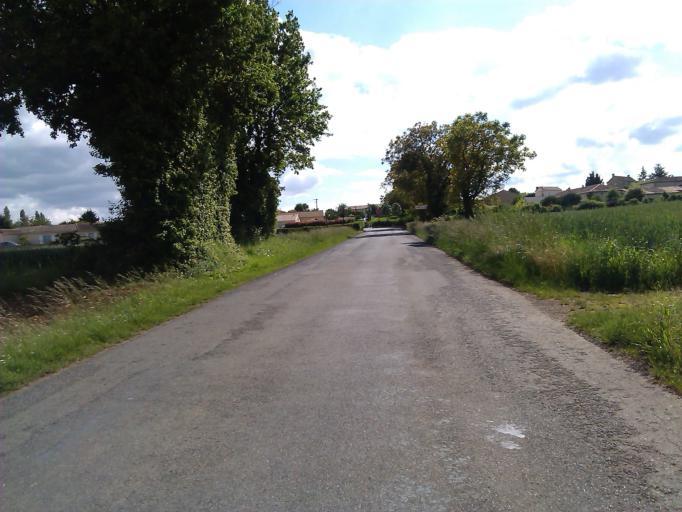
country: FR
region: Poitou-Charentes
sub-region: Departement de la Charente
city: Mansle
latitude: 45.8960
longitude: 0.2059
